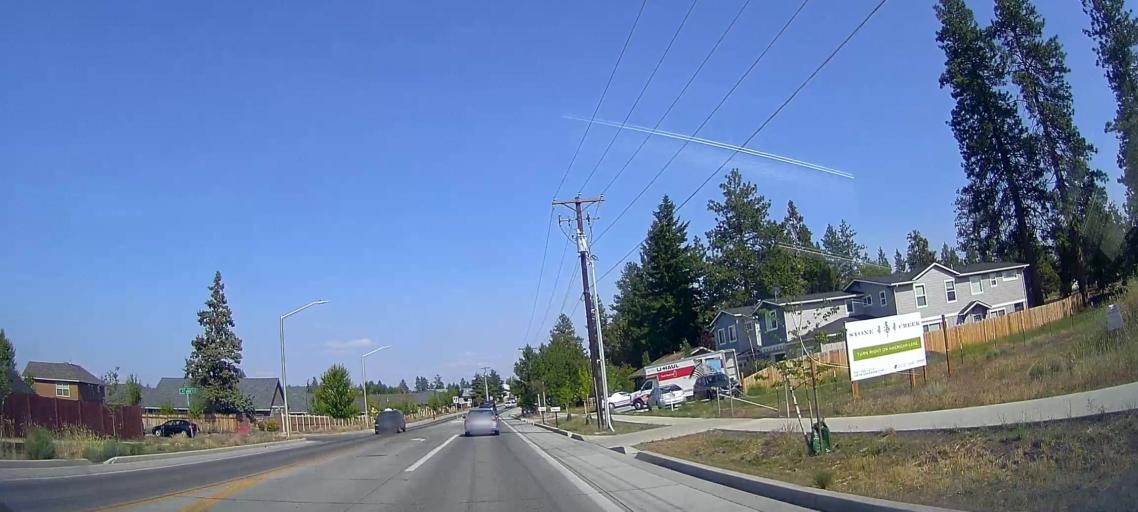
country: US
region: Oregon
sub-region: Deschutes County
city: Bend
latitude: 44.0385
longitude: -121.2961
